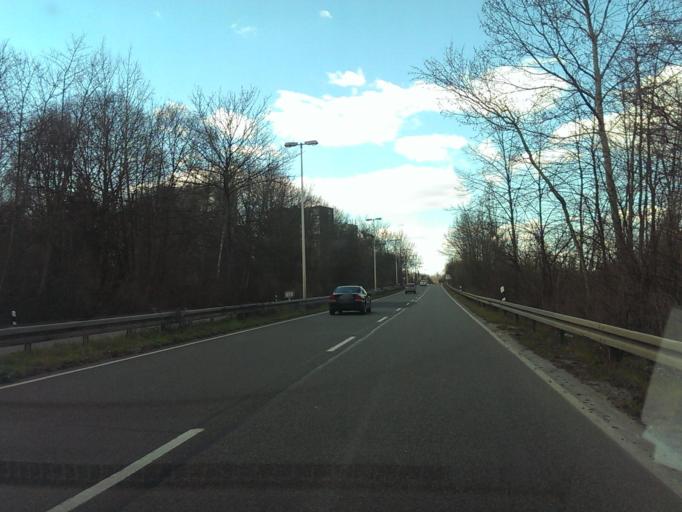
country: DE
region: Lower Saxony
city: Hildesheim
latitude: 52.1344
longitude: 9.9473
